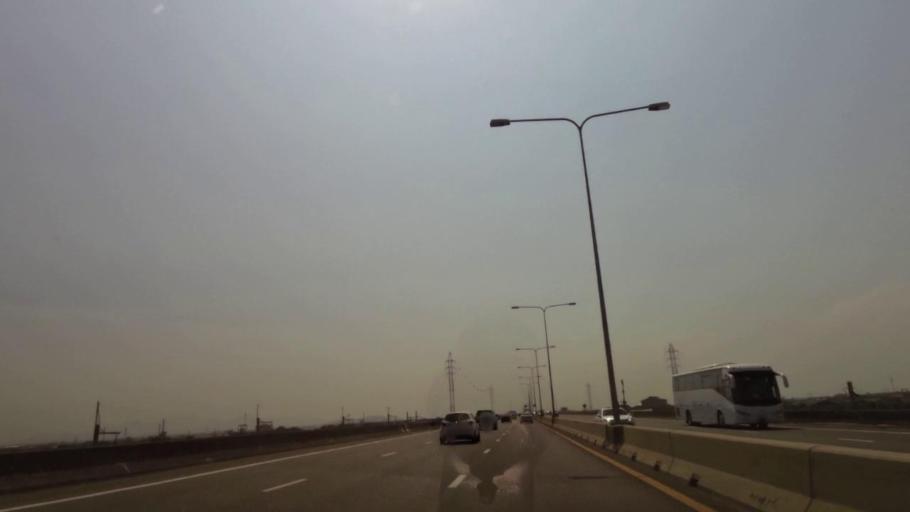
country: TH
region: Chachoengsao
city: Bang Pakong
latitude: 13.4897
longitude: 101.0059
